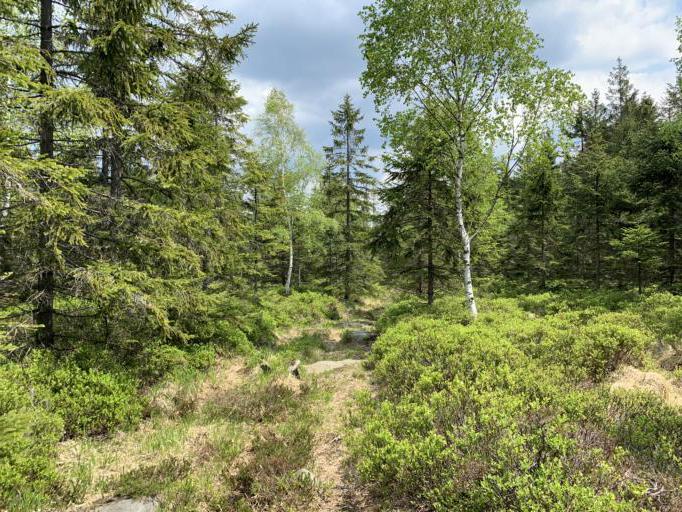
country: PL
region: Lower Silesian Voivodeship
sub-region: Powiat klodzki
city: Radkow
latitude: 50.4572
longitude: 16.3603
